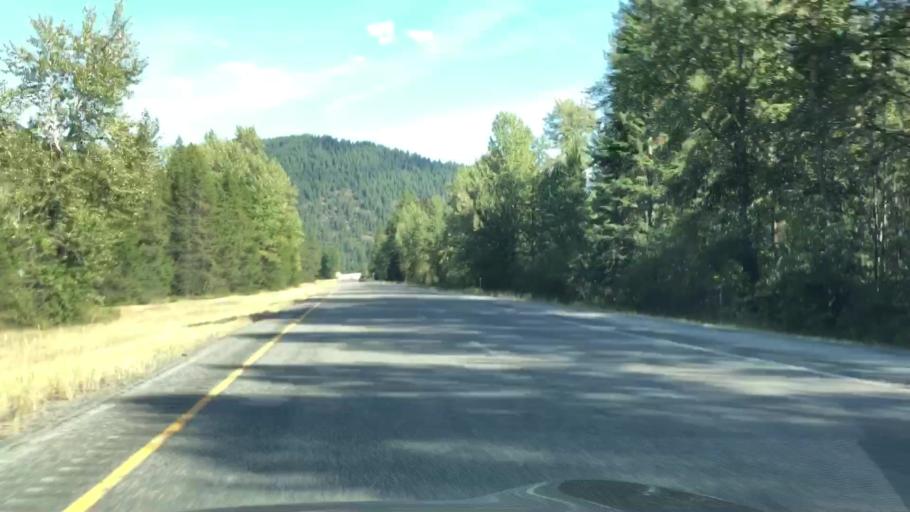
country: US
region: Montana
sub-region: Sanders County
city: Thompson Falls
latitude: 47.3584
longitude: -115.3094
